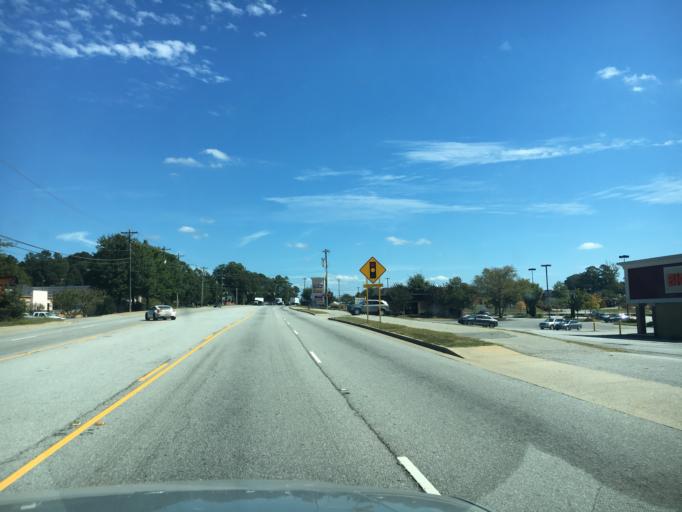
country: US
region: South Carolina
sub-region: Spartanburg County
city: Spartanburg
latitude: 34.9203
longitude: -81.8901
